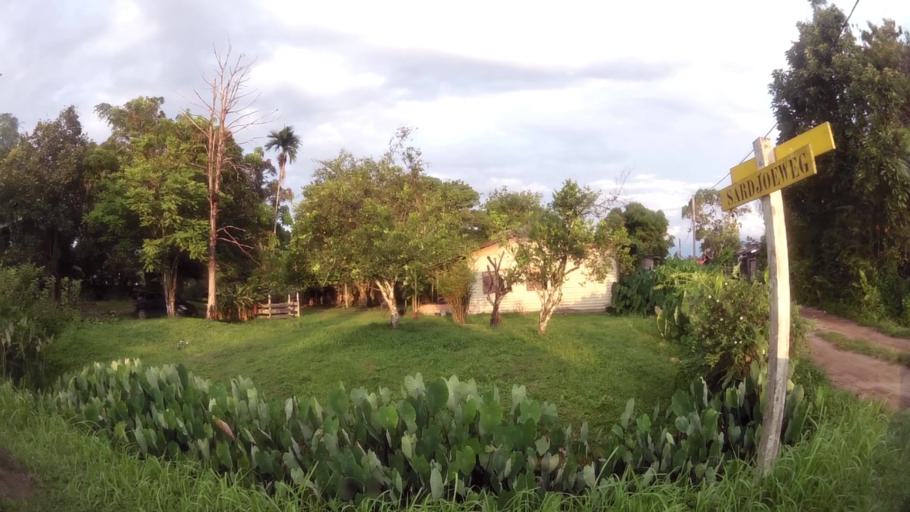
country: SR
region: Paramaribo
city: Paramaribo
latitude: 5.7820
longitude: -55.1662
